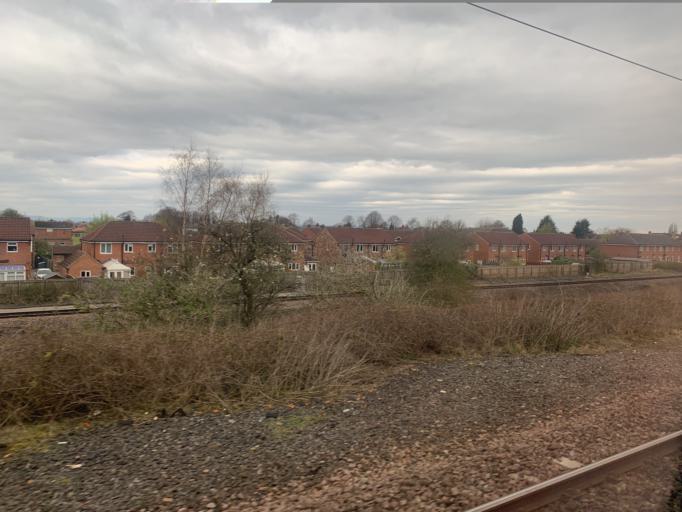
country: GB
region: England
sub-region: North Yorkshire
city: Northallerton
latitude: 54.3293
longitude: -1.4395
